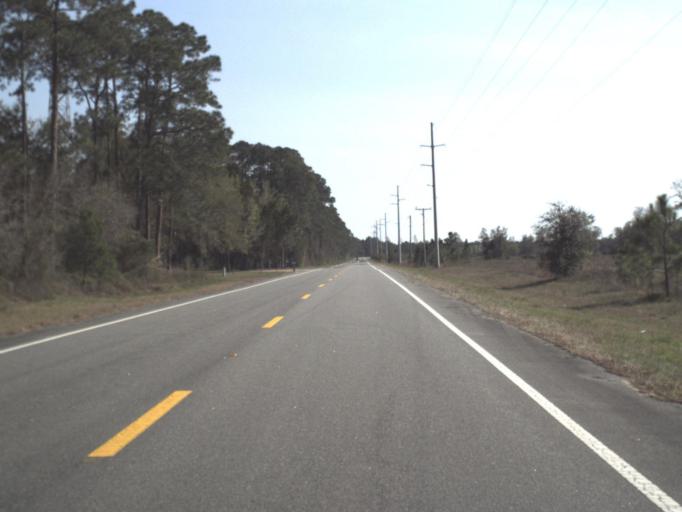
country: US
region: Florida
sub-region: Franklin County
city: Carrabelle
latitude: 29.9505
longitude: -84.5036
